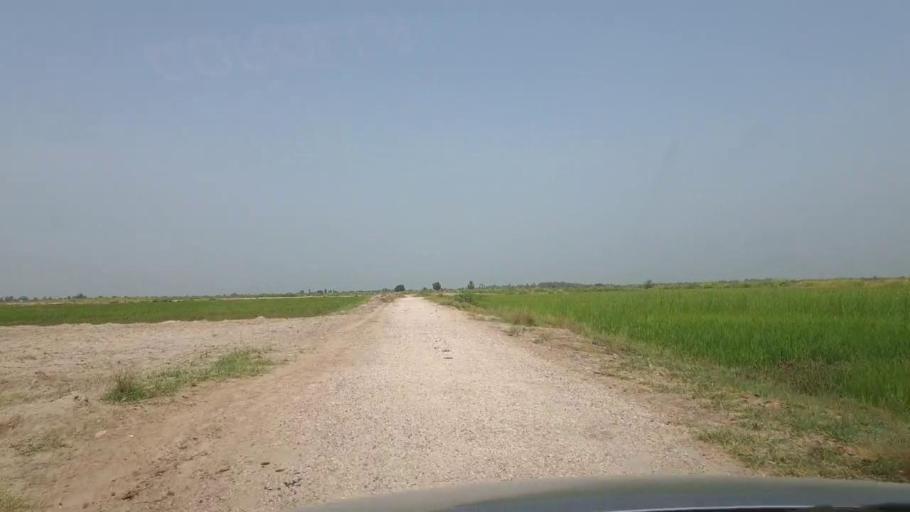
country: PK
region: Sindh
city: Madeji
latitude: 27.8136
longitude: 68.5157
